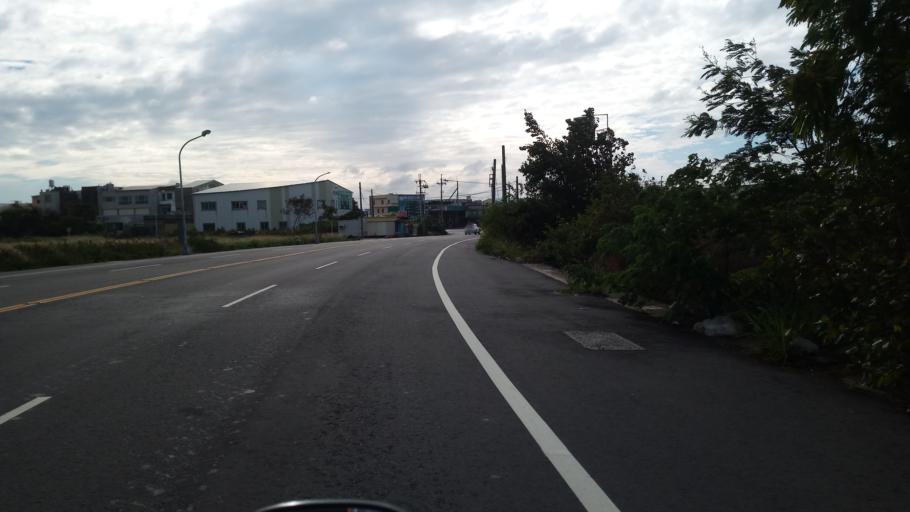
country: TW
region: Taiwan
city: Fengyuan
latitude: 24.3891
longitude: 120.6526
